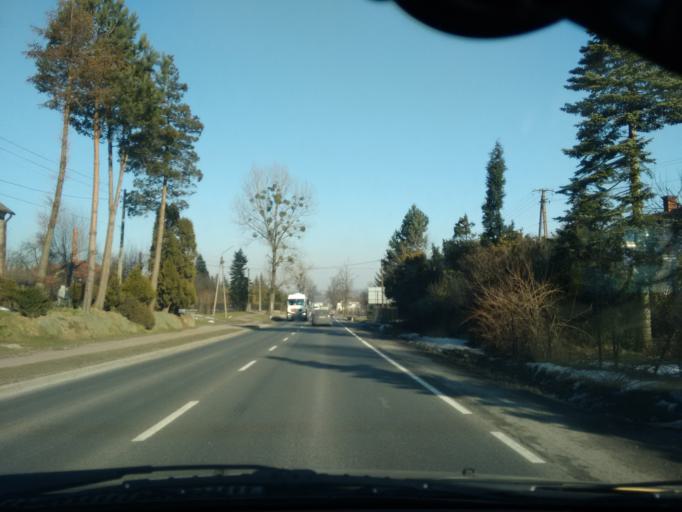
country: PL
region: Lesser Poland Voivodeship
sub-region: Powiat wadowicki
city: Inwald
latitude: 49.8656
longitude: 19.4045
